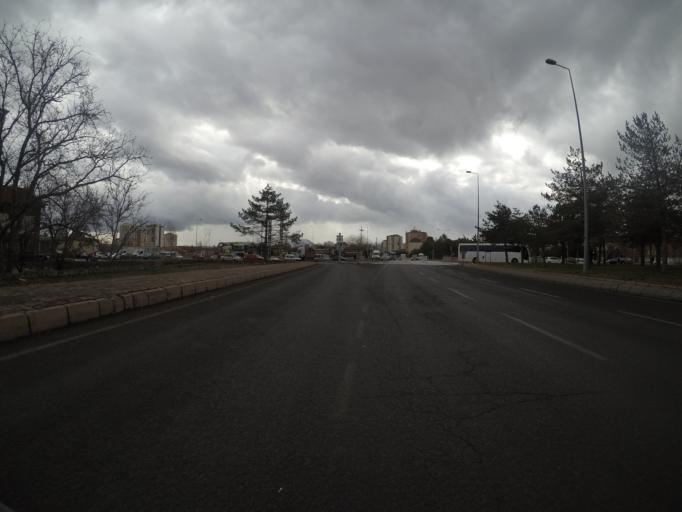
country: TR
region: Kayseri
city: Melikgazi
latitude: 38.7508
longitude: 35.4710
